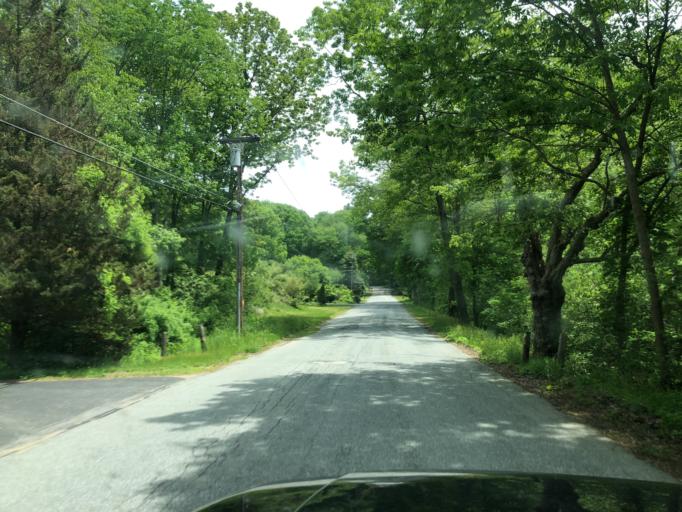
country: US
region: Connecticut
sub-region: Windham County
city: Thompson
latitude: 41.9639
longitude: -71.8582
